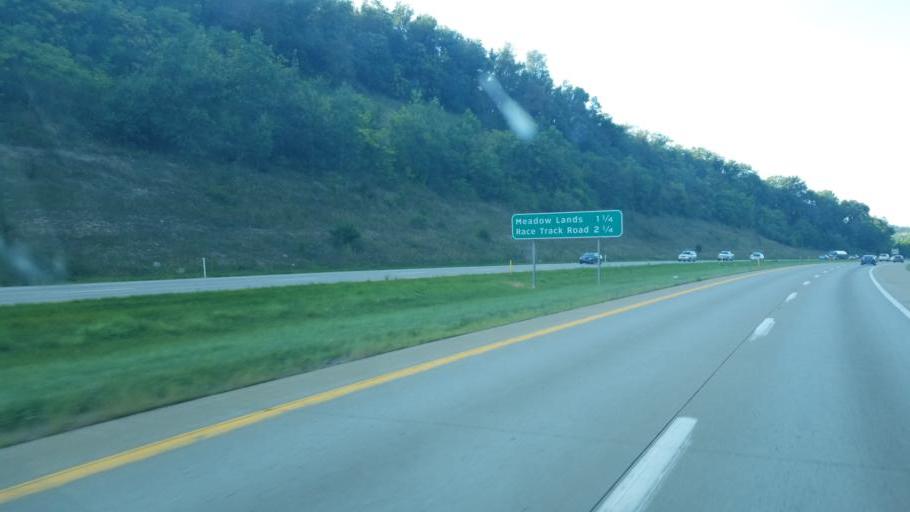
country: US
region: Pennsylvania
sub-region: Washington County
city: Washington
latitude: 40.2018
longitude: -80.2486
